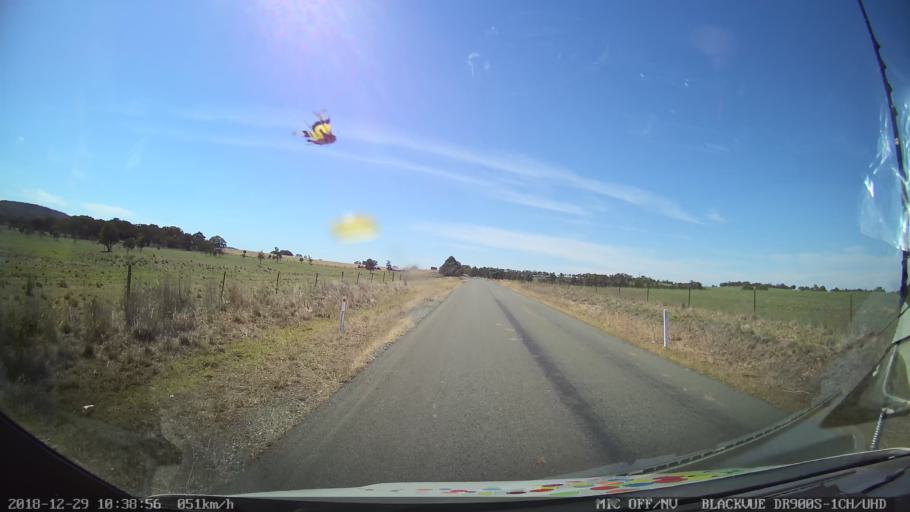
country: AU
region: New South Wales
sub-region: Yass Valley
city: Gundaroo
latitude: -35.0018
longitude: 149.5082
